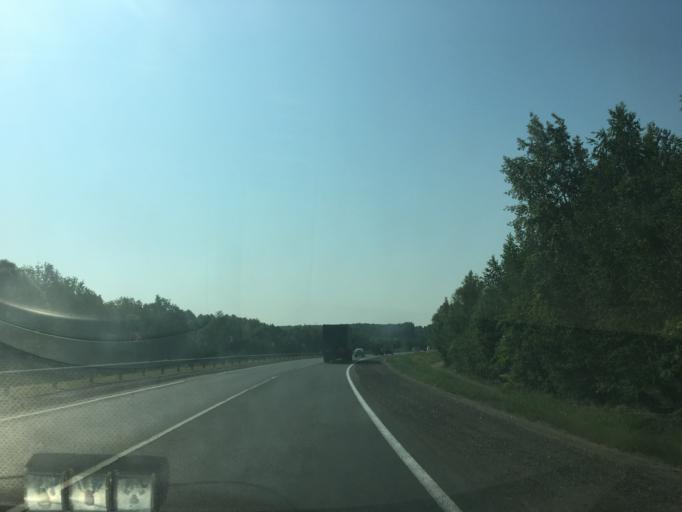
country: RU
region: Nizjnij Novgorod
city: Pamyat' Parizhskoy Kommuny
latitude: 56.0768
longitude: 44.3699
